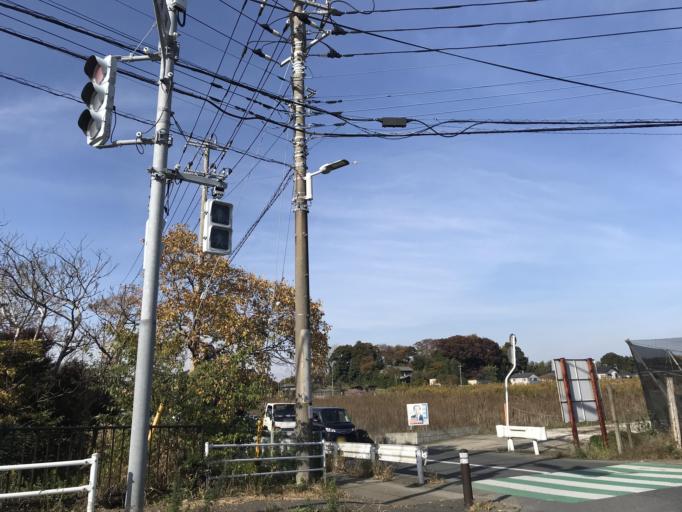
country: JP
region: Chiba
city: Shiroi
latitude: 35.7830
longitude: 139.9946
